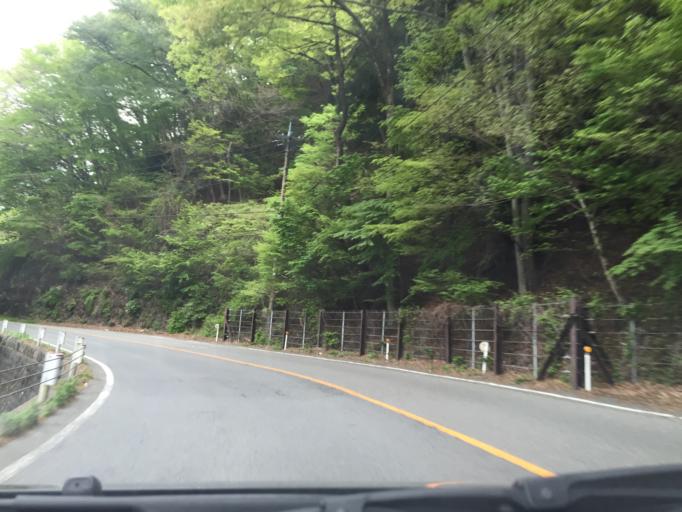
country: JP
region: Tochigi
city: Nikko
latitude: 36.8656
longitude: 139.7138
